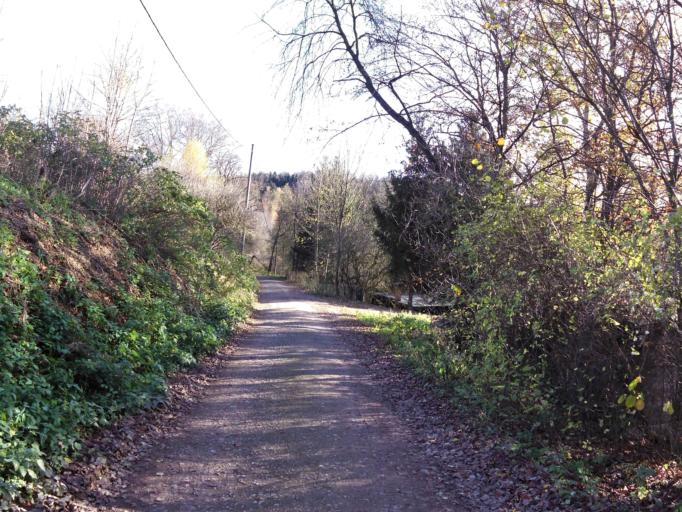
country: DE
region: Thuringia
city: Ruhla
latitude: 50.8831
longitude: 10.3945
